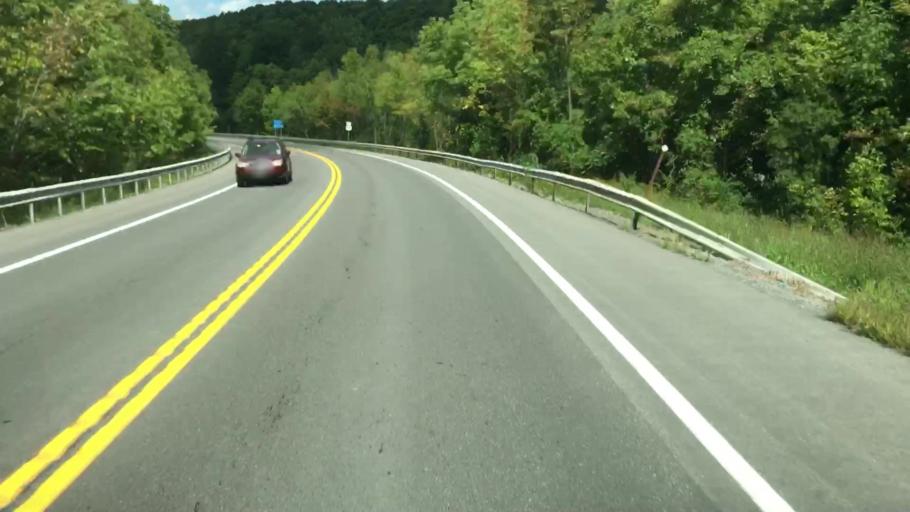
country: US
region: New York
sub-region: Onondaga County
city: Marcellus
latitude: 42.9608
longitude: -76.3356
